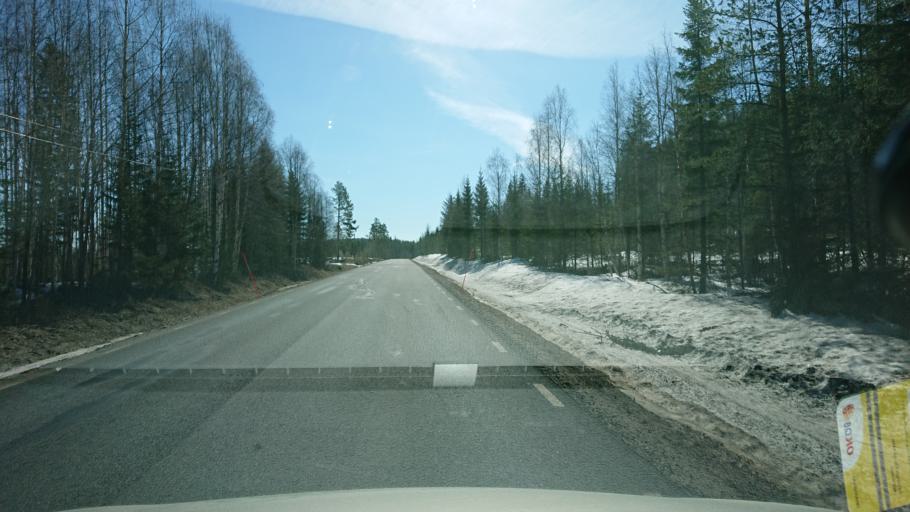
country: SE
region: Vaesterbotten
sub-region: Dorotea Kommun
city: Dorotea
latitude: 64.0998
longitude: 16.2484
